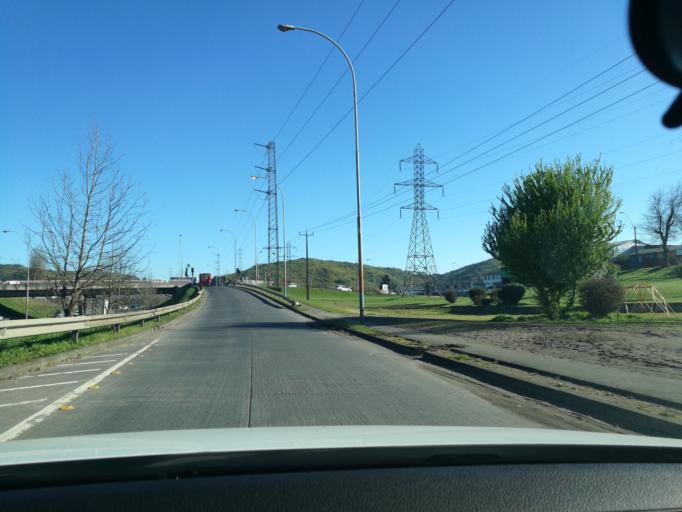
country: CL
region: Biobio
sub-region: Provincia de Concepcion
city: Concepcion
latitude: -36.8040
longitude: -73.0394
